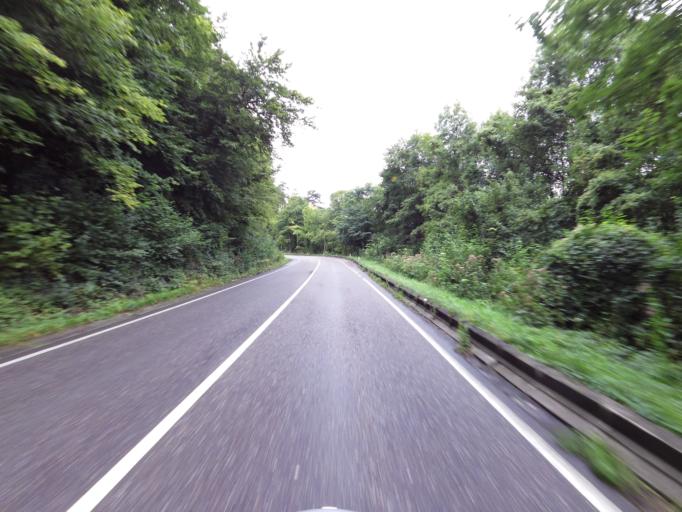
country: BE
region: Wallonia
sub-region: Province de Namur
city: Rochefort
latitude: 50.1427
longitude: 5.1883
